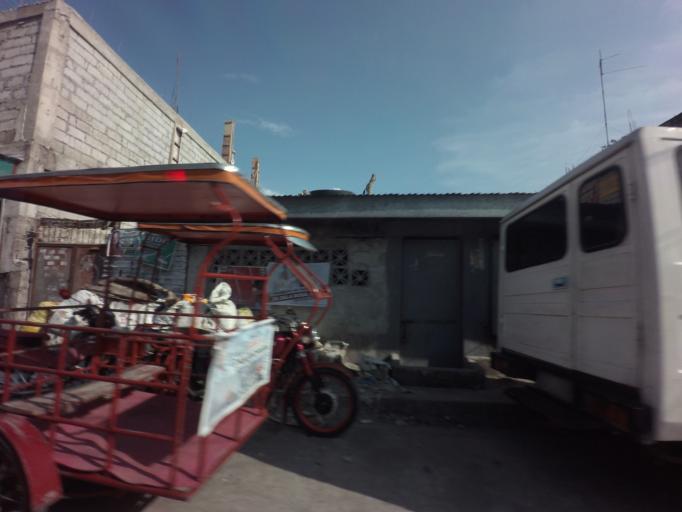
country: PH
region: Calabarzon
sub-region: Province of Rizal
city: Taguig
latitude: 14.4990
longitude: 121.0579
